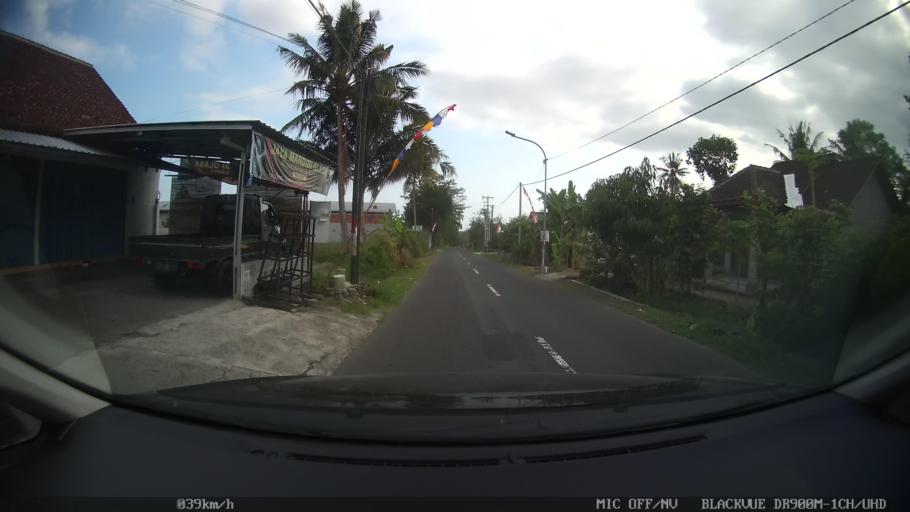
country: ID
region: Daerah Istimewa Yogyakarta
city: Melati
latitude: -7.6864
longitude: 110.4232
